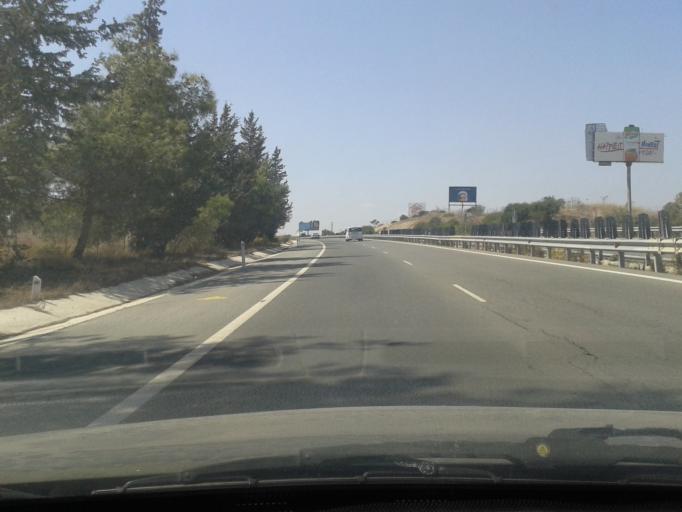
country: CY
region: Limassol
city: Pyrgos
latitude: 34.7336
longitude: 33.2196
